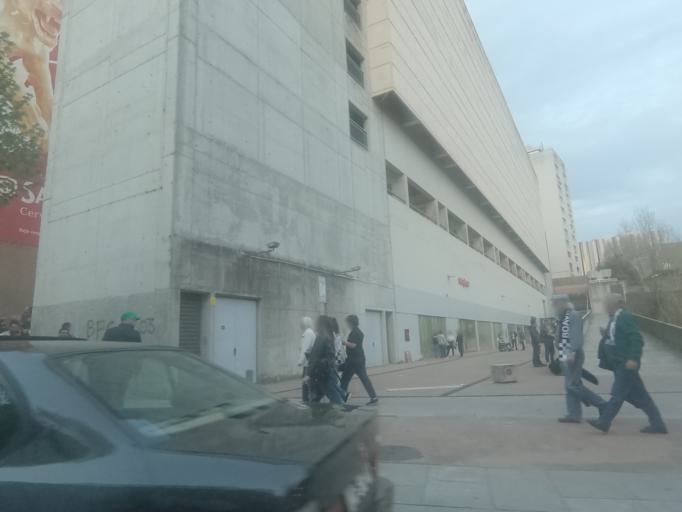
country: PT
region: Porto
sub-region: Matosinhos
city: Senhora da Hora
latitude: 41.1615
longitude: -8.6435
